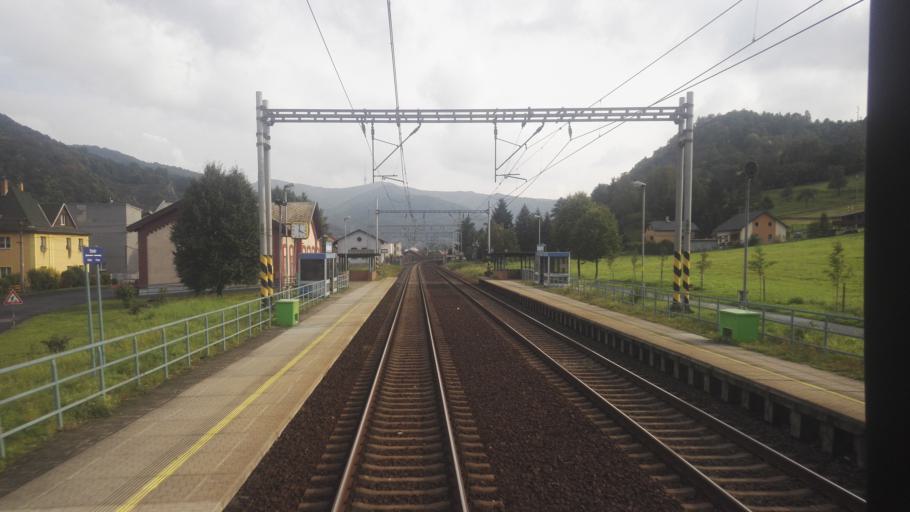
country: CZ
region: Ustecky
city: Povrly
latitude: 50.7162
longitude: 14.1913
